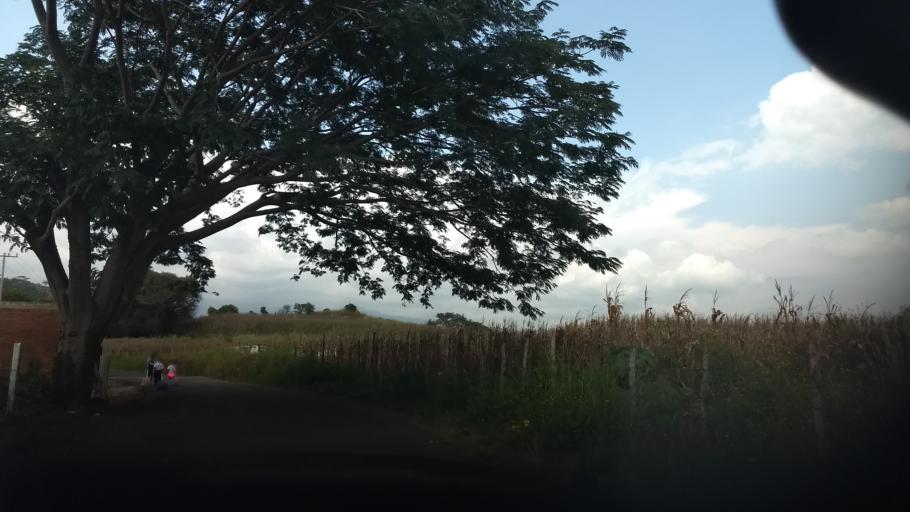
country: MX
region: Jalisco
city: Tonila
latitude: 19.4094
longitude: -103.4857
